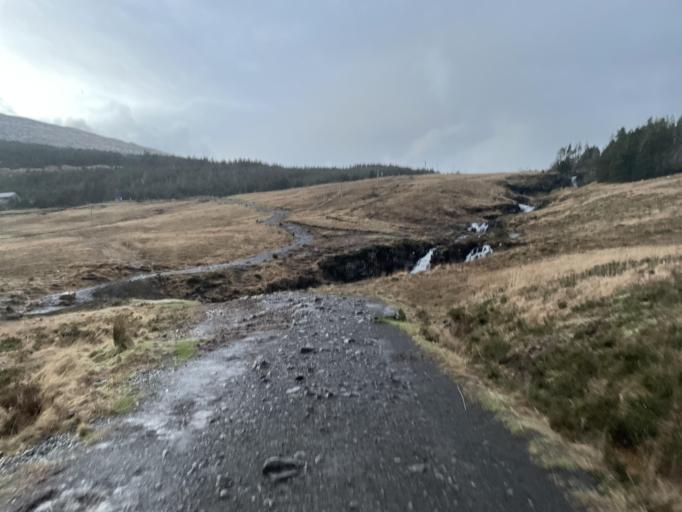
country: GB
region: Scotland
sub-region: Highland
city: Isle of Skye
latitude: 57.2500
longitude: -6.2677
